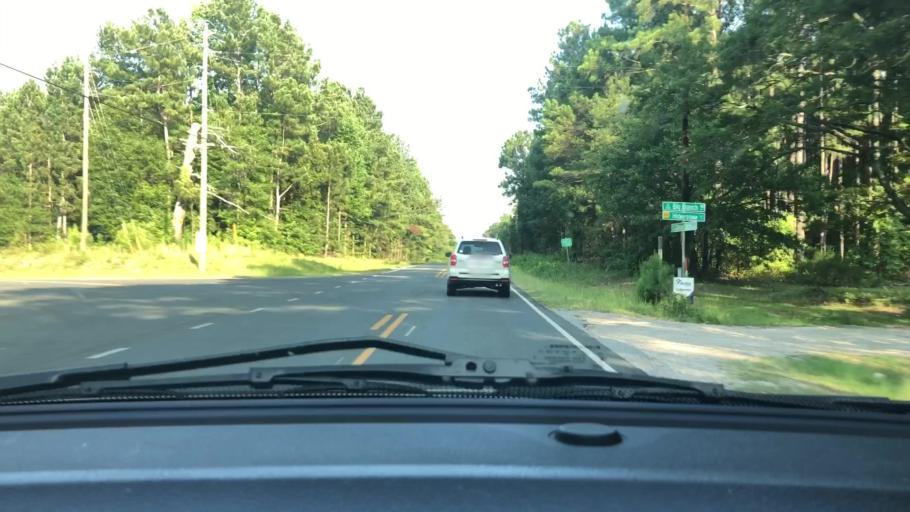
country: US
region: North Carolina
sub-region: Lee County
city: Broadway
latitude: 35.3607
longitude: -79.0861
